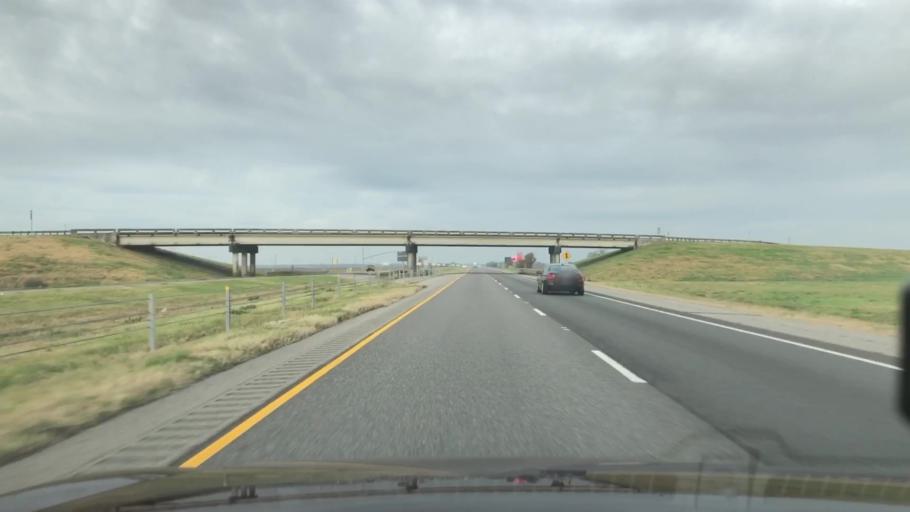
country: US
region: Mississippi
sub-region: Warren County
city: Vicksburg
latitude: 32.3240
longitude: -90.9562
